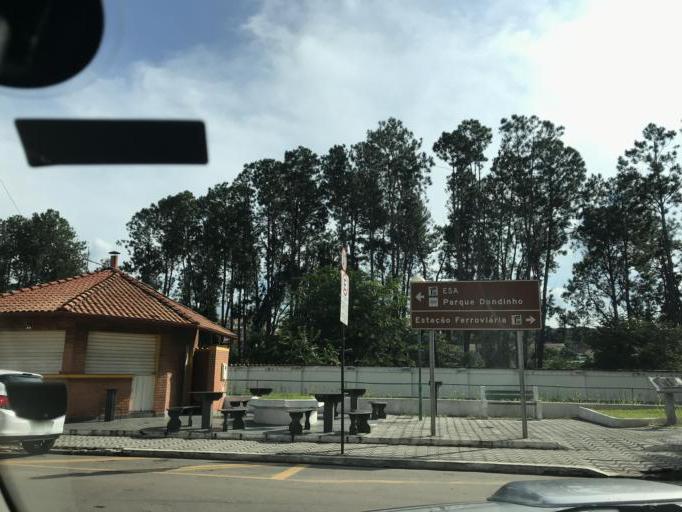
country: BR
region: Minas Gerais
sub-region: Tres Coracoes
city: Tres Coracoes
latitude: -21.7005
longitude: -45.2581
